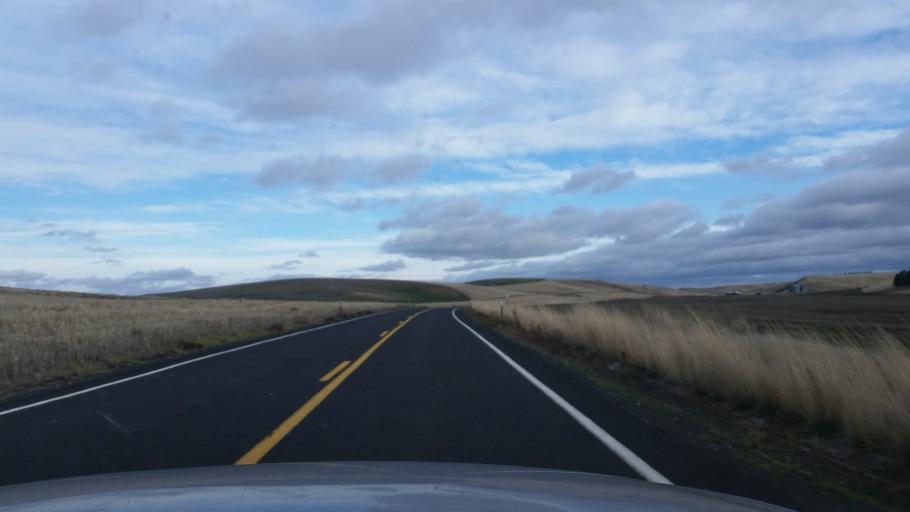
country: US
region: Washington
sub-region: Lincoln County
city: Davenport
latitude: 47.3574
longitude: -118.0516
